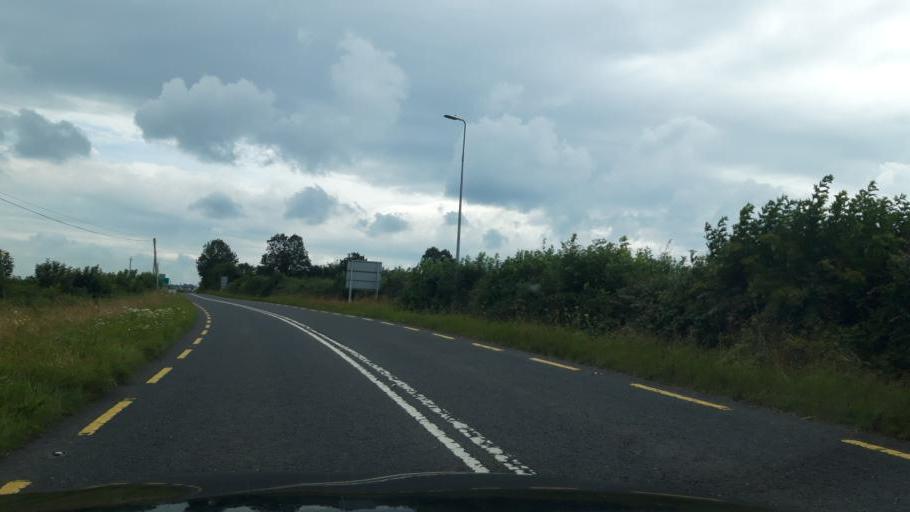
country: IE
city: Ballylinan
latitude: 52.9281
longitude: -7.0616
